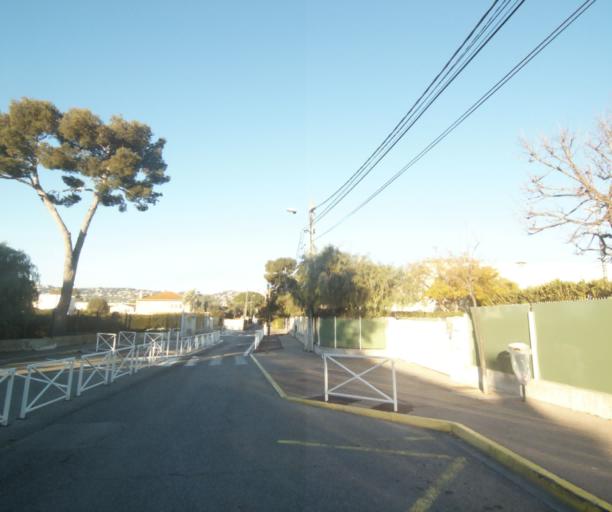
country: FR
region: Provence-Alpes-Cote d'Azur
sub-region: Departement des Alpes-Maritimes
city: Antibes
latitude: 43.5765
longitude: 7.0936
